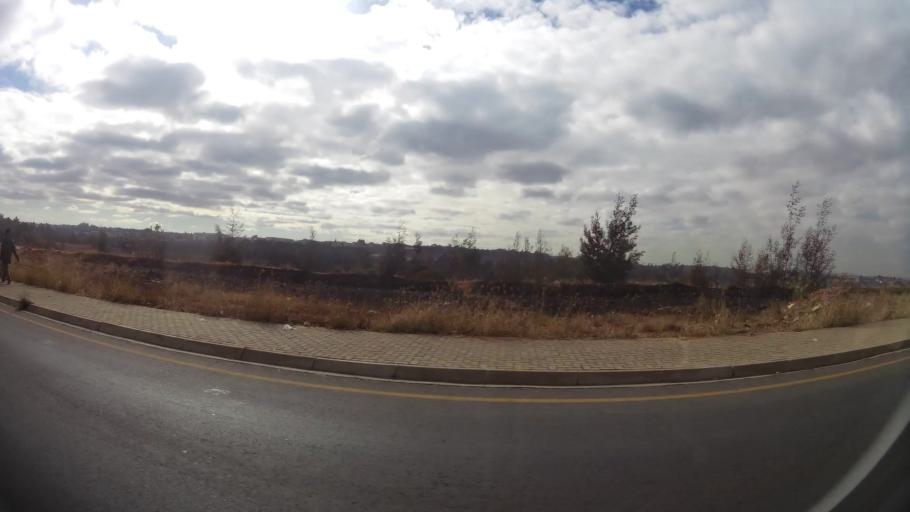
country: ZA
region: Gauteng
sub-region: City of Johannesburg Metropolitan Municipality
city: Roodepoort
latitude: -26.2003
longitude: 27.9036
